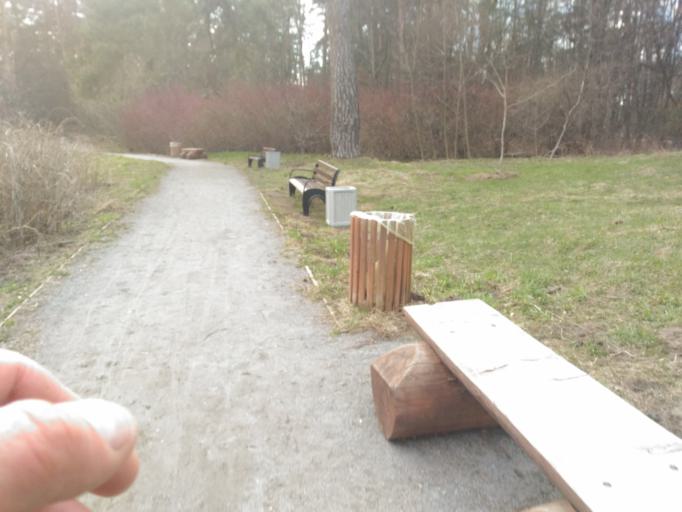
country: RU
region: Moscow
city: Shchukino
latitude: 55.7830
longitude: 37.4244
